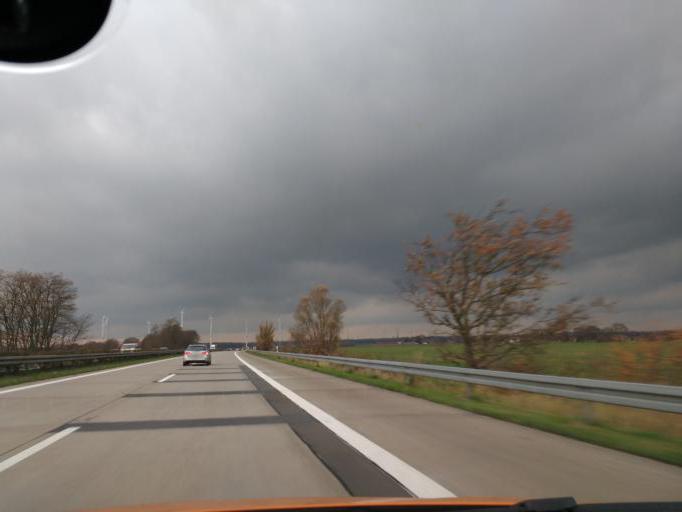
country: DE
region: Brandenburg
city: Heiligengrabe
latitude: 53.1748
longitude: 12.3172
